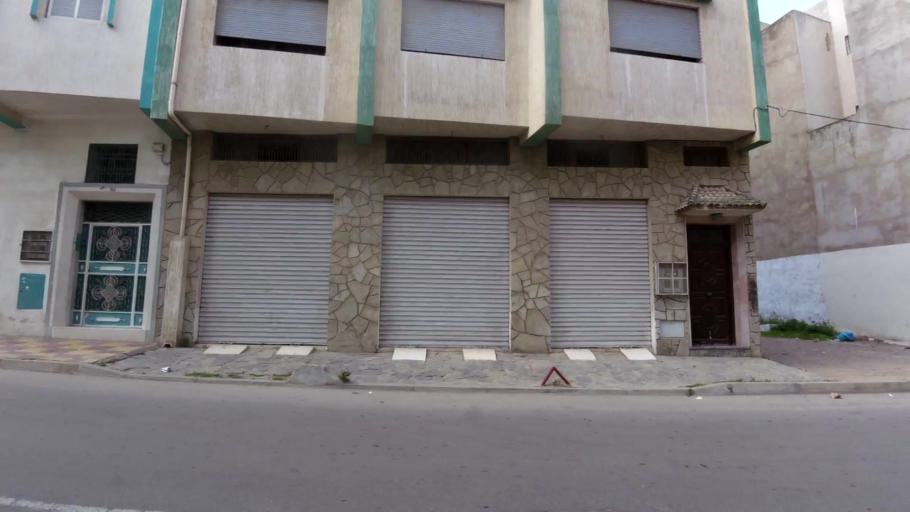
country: MA
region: Tanger-Tetouan
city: Tetouan
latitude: 35.5856
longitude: -5.3511
